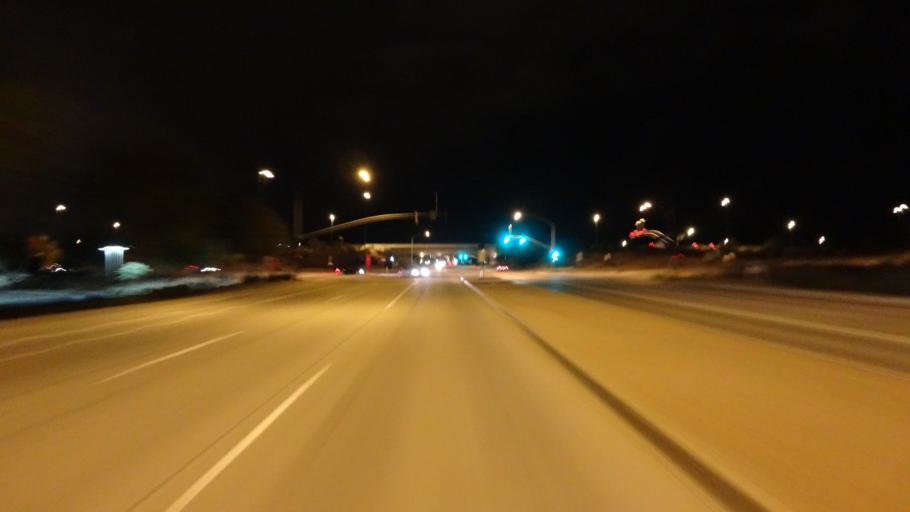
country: US
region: Arizona
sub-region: Pinal County
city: Apache Junction
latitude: 33.3854
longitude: -111.5981
